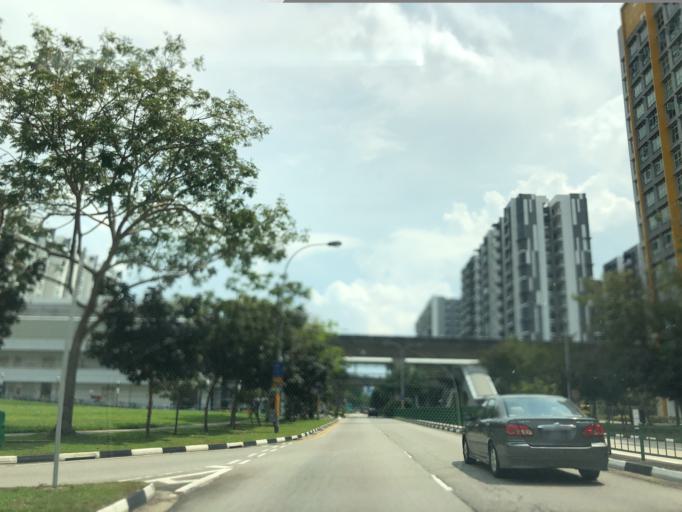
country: MY
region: Johor
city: Kampung Pasir Gudang Baru
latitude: 1.3910
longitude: 103.8941
